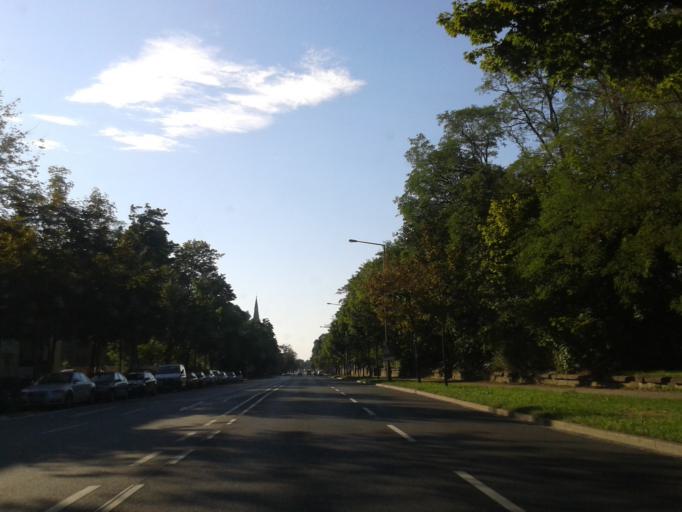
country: DE
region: Saxony
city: Albertstadt
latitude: 51.0720
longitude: 13.7693
